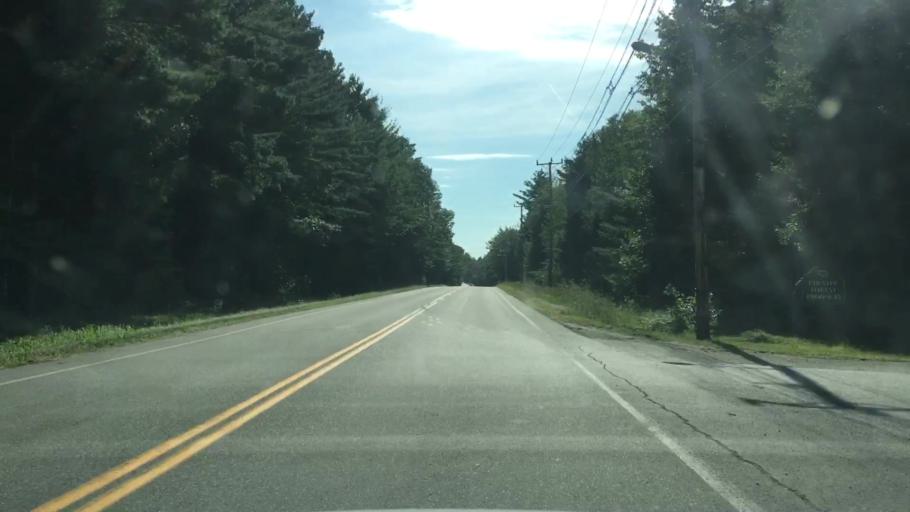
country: US
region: Maine
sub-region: Penobscot County
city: Lincoln
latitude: 45.3909
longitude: -68.5322
